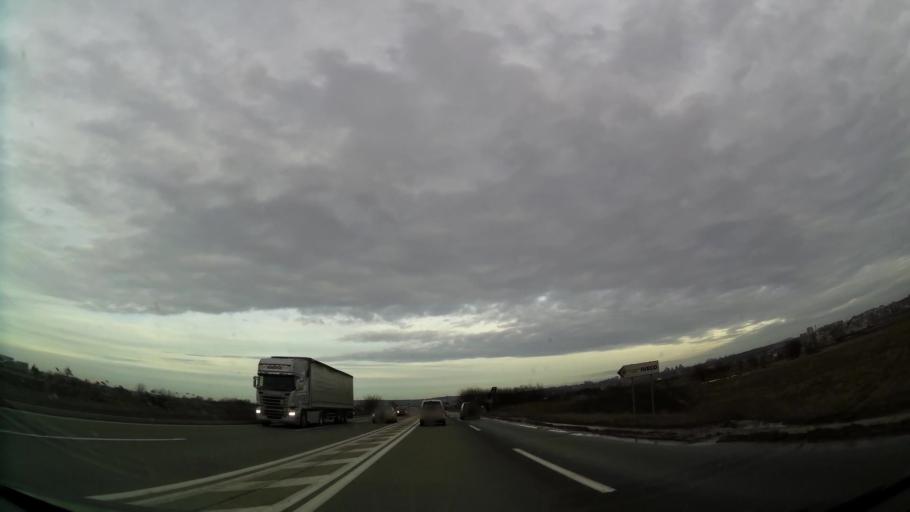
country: RS
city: Ostruznica
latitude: 44.7409
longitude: 20.3555
